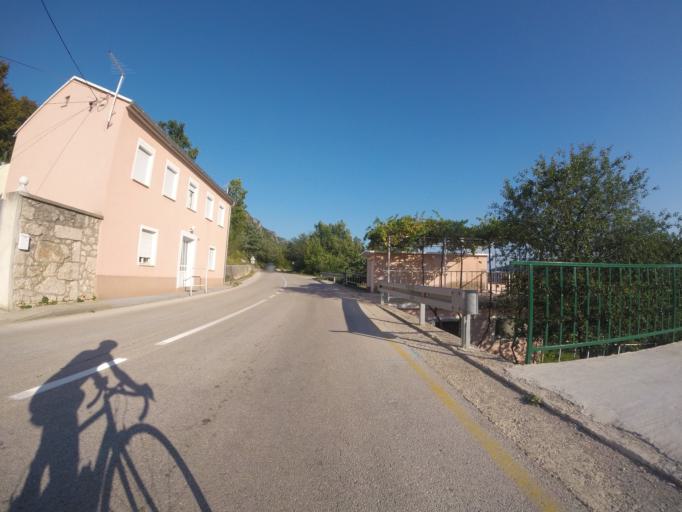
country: HR
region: Primorsko-Goranska
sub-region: Grad Crikvenica
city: Crikvenica
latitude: 45.1920
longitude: 14.7248
